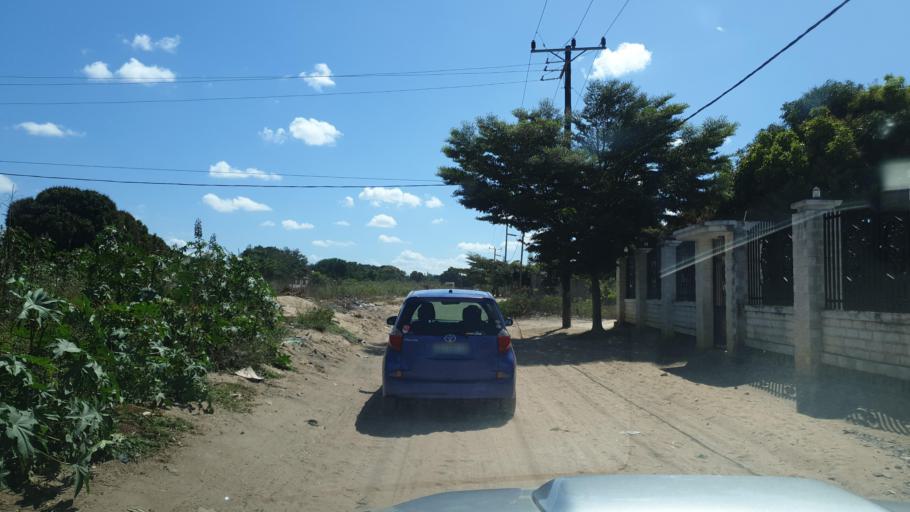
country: MZ
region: Nampula
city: Nampula
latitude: -15.1043
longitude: 39.2061
